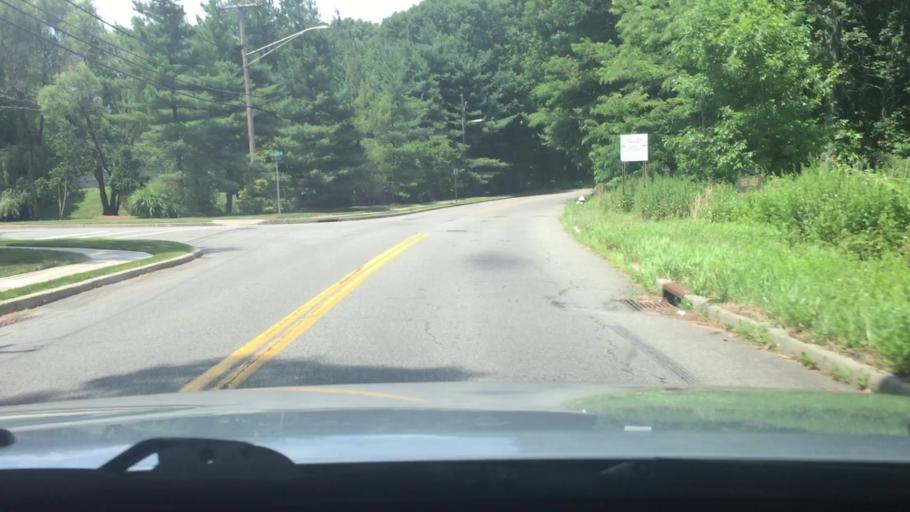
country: US
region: New Jersey
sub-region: Middlesex County
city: East Brunswick
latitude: 40.4109
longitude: -74.4075
